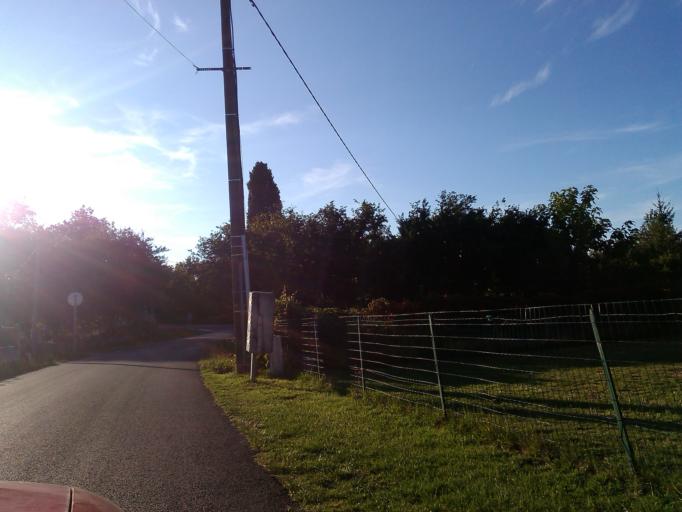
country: FR
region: Aquitaine
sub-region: Departement de la Gironde
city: Soulac-sur-Mer
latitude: 45.4331
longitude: -1.0457
